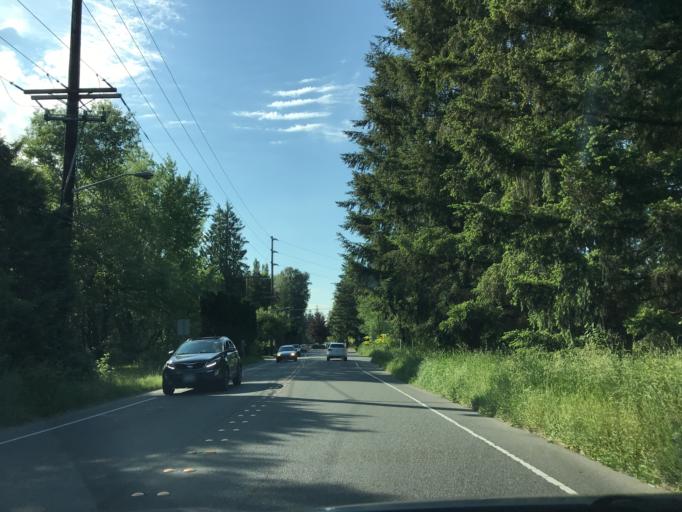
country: US
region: Washington
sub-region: King County
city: Issaquah
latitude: 47.5149
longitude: -122.0251
